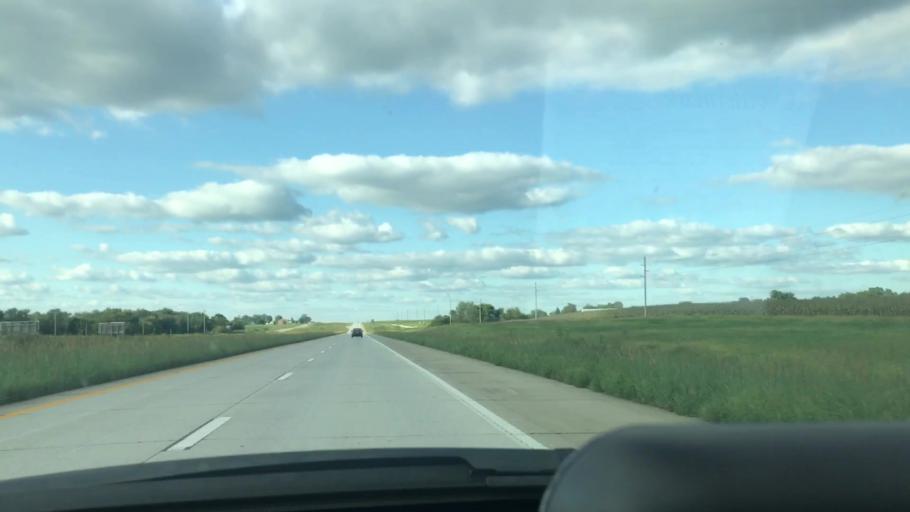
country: US
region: Missouri
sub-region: Benton County
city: Cole Camp
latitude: 38.4916
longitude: -93.2736
